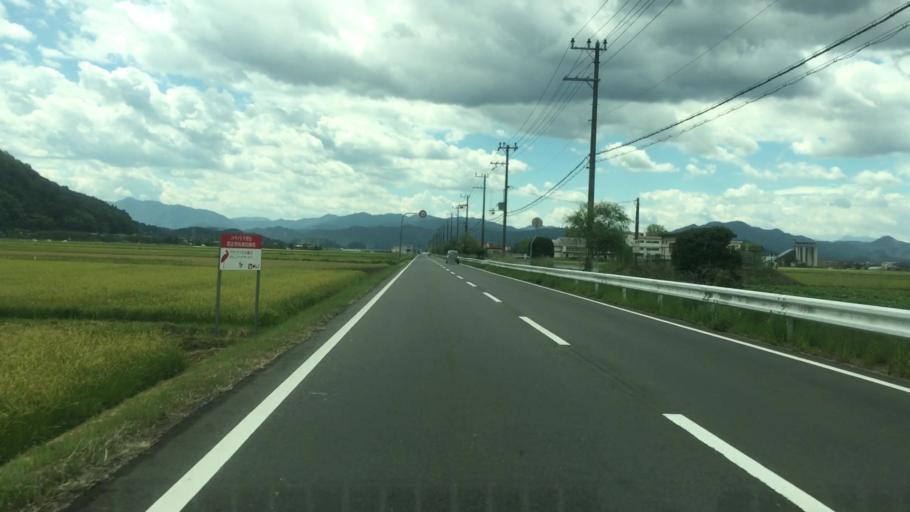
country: JP
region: Hyogo
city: Toyooka
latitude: 35.5347
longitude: 134.8397
